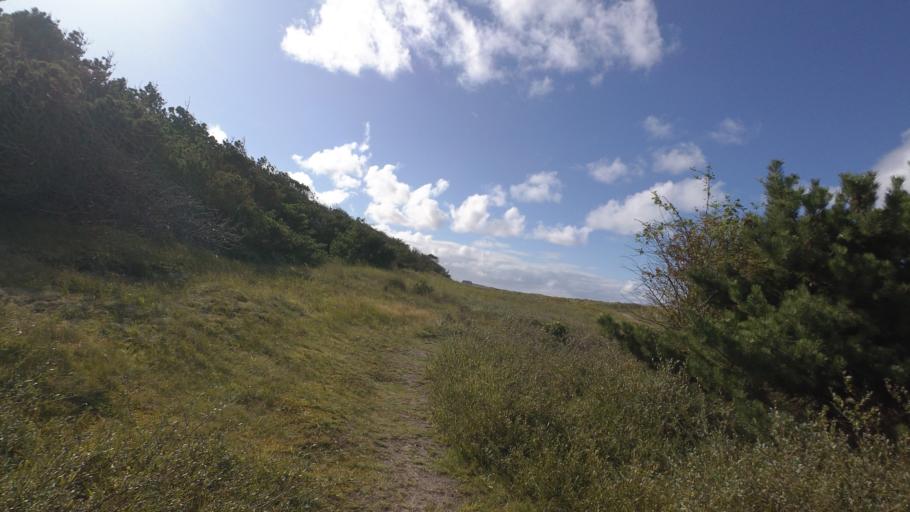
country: NL
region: Friesland
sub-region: Gemeente Ameland
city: Nes
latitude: 53.4601
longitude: 5.8213
